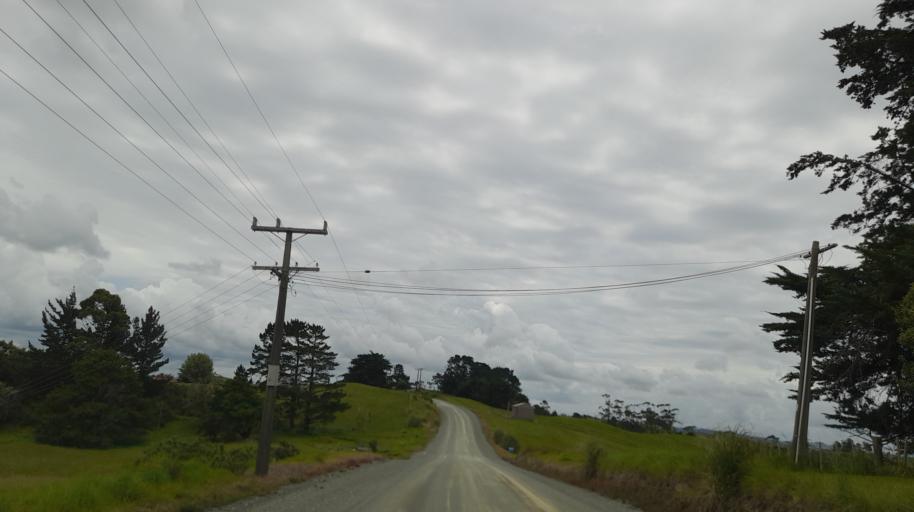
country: NZ
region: Auckland
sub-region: Auckland
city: Wellsford
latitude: -36.2507
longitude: 174.4171
